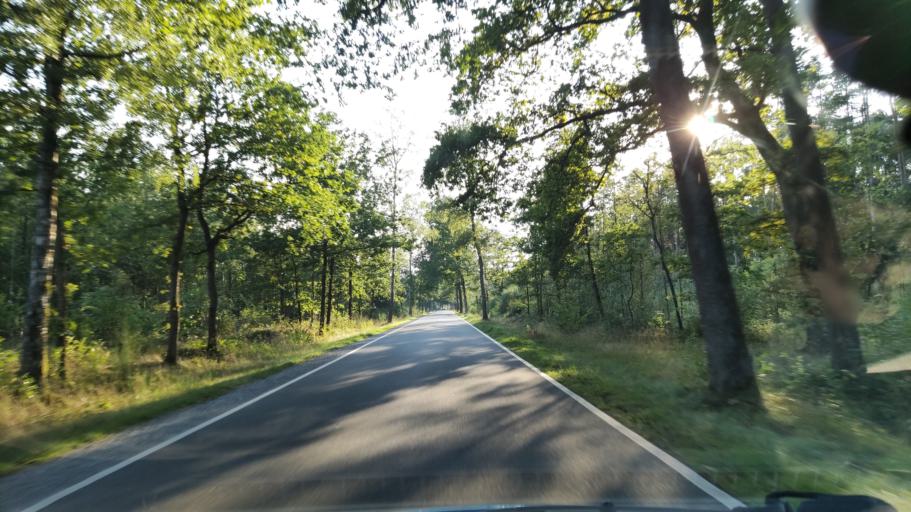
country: DE
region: Lower Saxony
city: Fassberg
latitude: 52.8932
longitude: 10.1873
